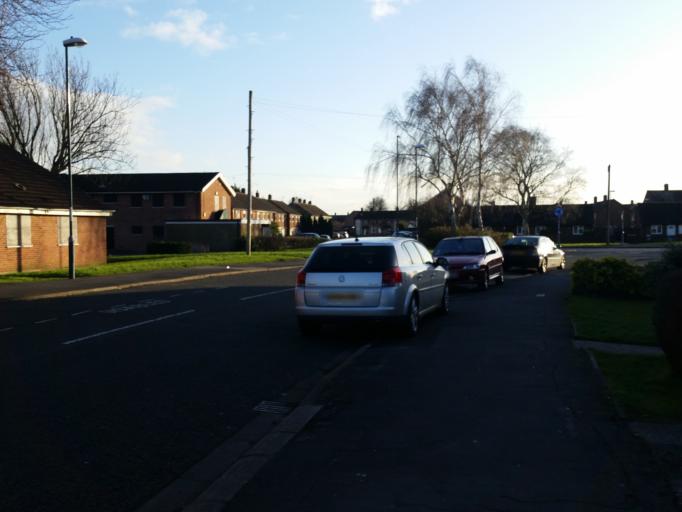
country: GB
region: England
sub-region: Derbyshire
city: Borrowash
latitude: 52.8877
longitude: -1.4193
